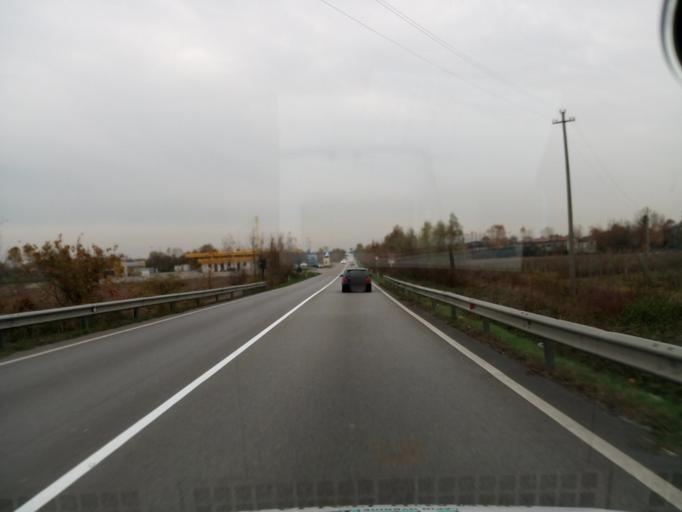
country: IT
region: Veneto
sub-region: Provincia di Venezia
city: Campolongo Maggiore Liettoli
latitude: 45.3549
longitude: 12.0071
